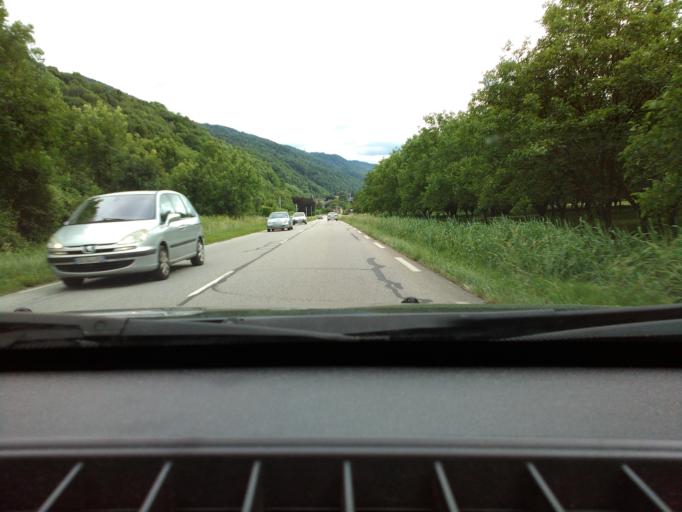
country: FR
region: Rhone-Alpes
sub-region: Departement de l'Isere
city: Tencin
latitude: 45.3187
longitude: 5.9656
